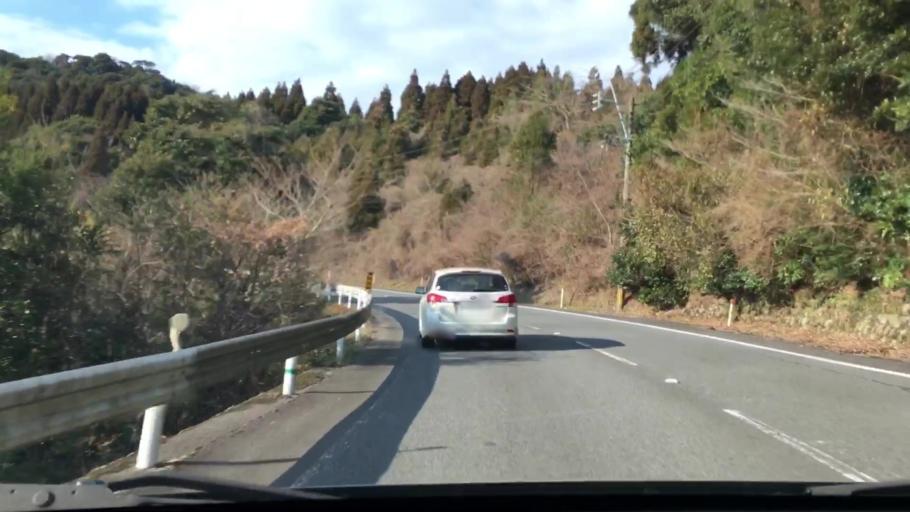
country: JP
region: Miyazaki
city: Miyazaki-shi
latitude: 31.7789
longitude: 131.3301
